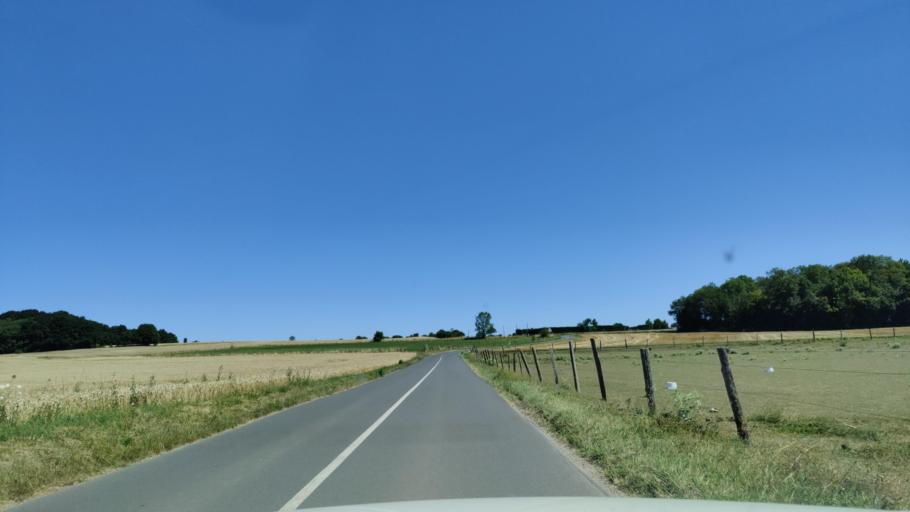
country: FR
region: Ile-de-France
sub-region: Departement de l'Essonne
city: Fontenay-les-Briis
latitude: 48.5981
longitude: 2.1620
